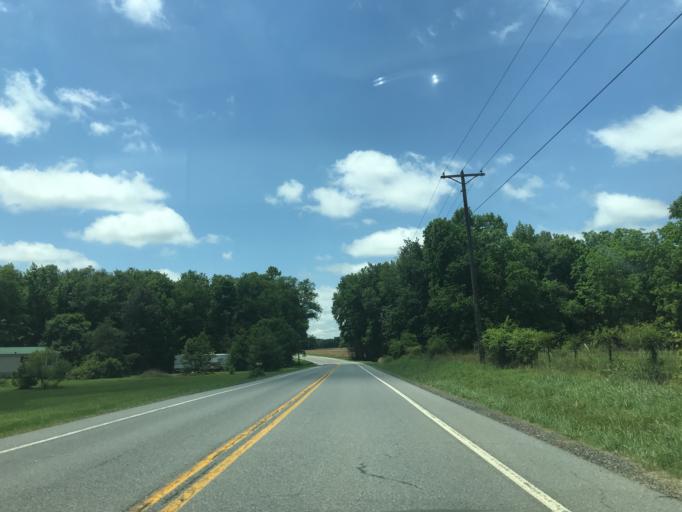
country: US
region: Maryland
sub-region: Caroline County
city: Federalsburg
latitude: 38.7339
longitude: -75.7280
